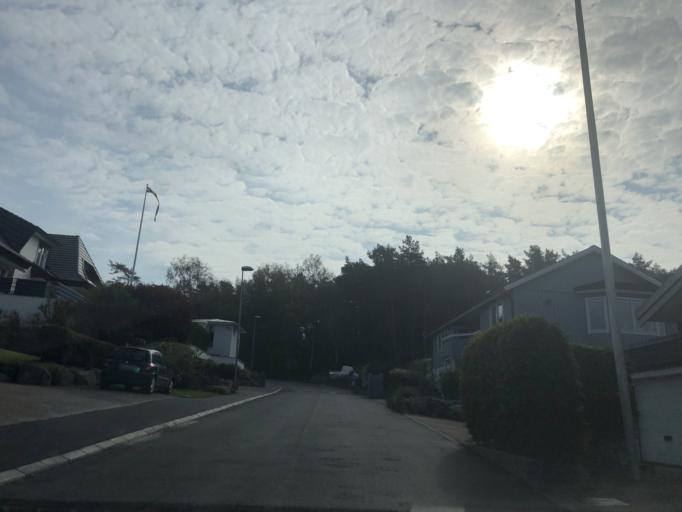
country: SE
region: Vaestra Goetaland
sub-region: Goteborg
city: Majorna
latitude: 57.6465
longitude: 11.8714
